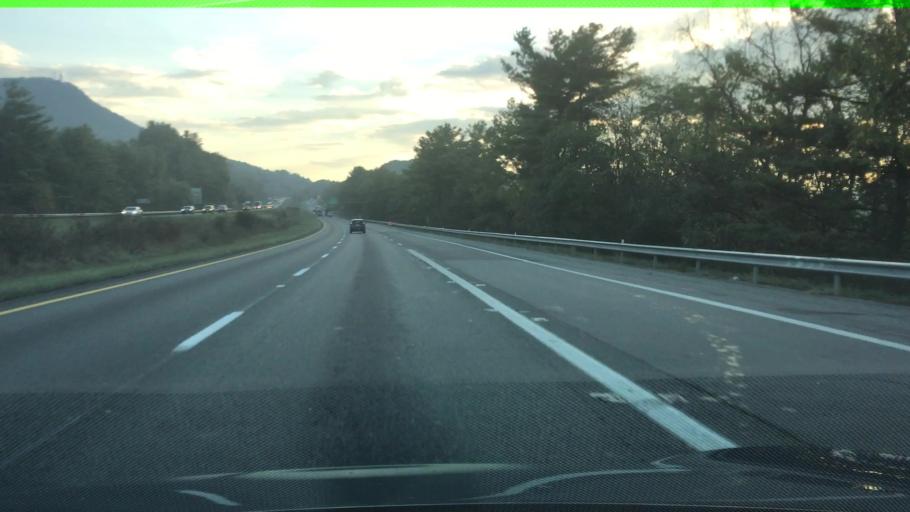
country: US
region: Virginia
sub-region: Roanoke County
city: Hollins
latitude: 37.3616
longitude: -79.9518
